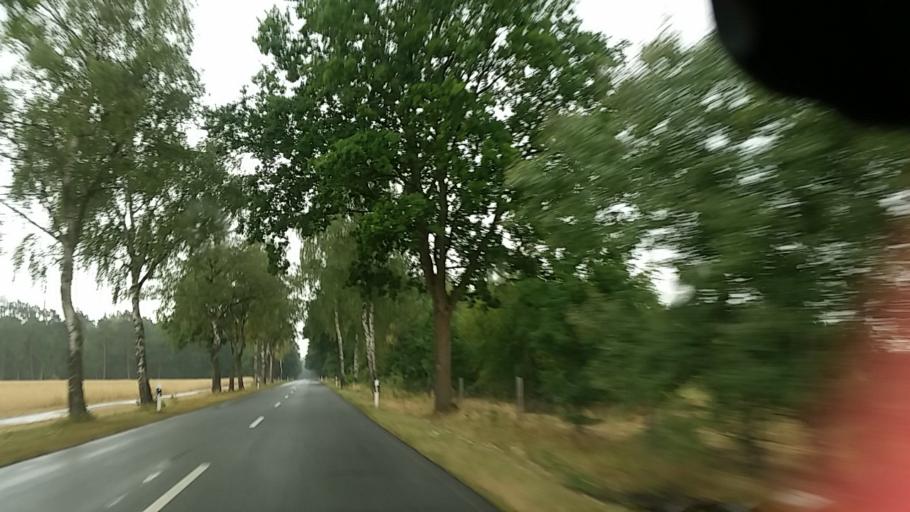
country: DE
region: Lower Saxony
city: Bokensdorf
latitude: 52.5356
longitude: 10.7173
